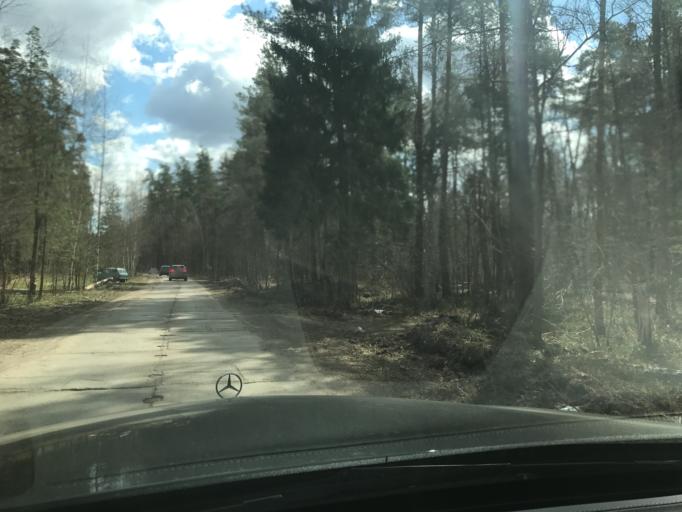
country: RU
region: Moskovskaya
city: Vereya
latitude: 55.8404
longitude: 39.1083
